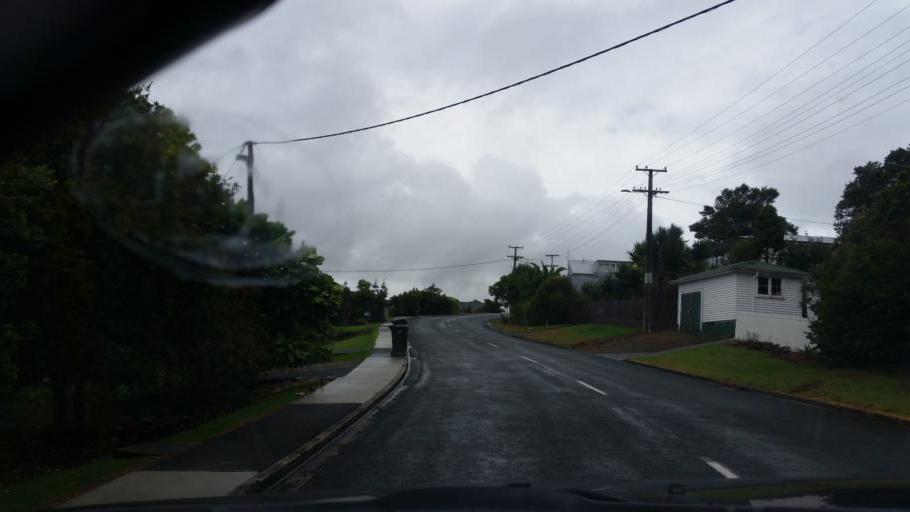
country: NZ
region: Northland
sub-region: Whangarei
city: Ruakaka
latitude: -36.1081
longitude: 174.3610
